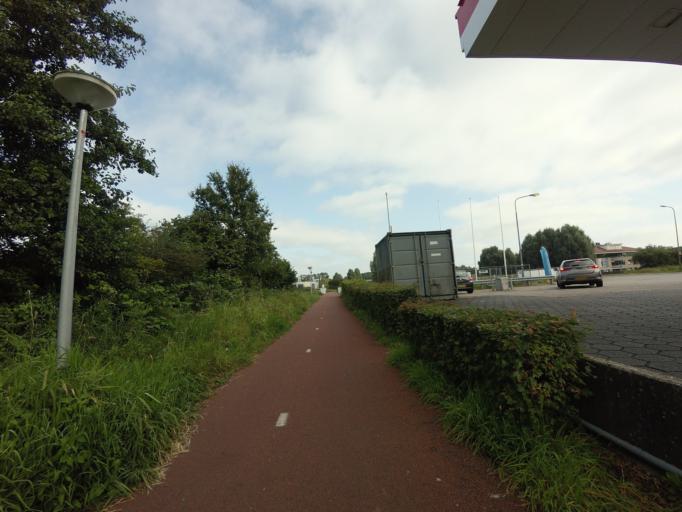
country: NL
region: Overijssel
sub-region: Gemeente Steenwijkerland
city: Steenwijk
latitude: 52.7971
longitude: 6.1238
